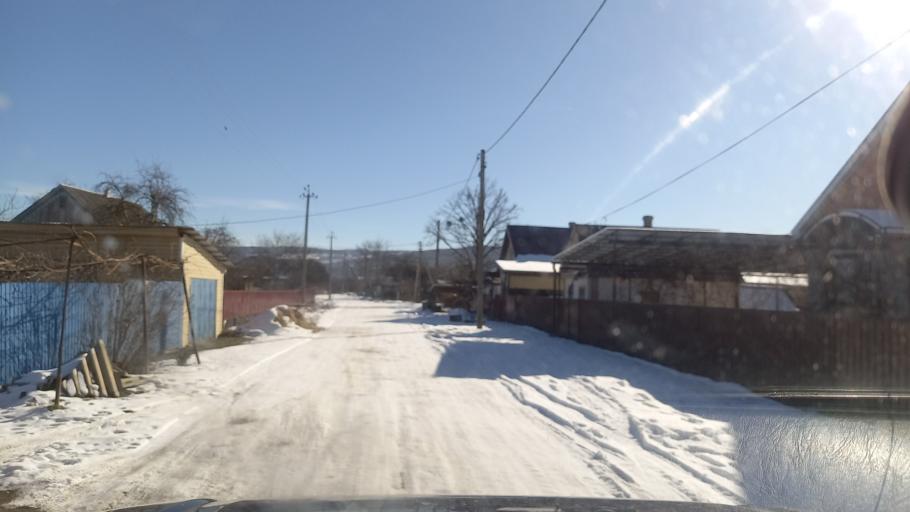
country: RU
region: Adygeya
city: Kamennomostskiy
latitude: 44.2986
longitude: 40.1700
